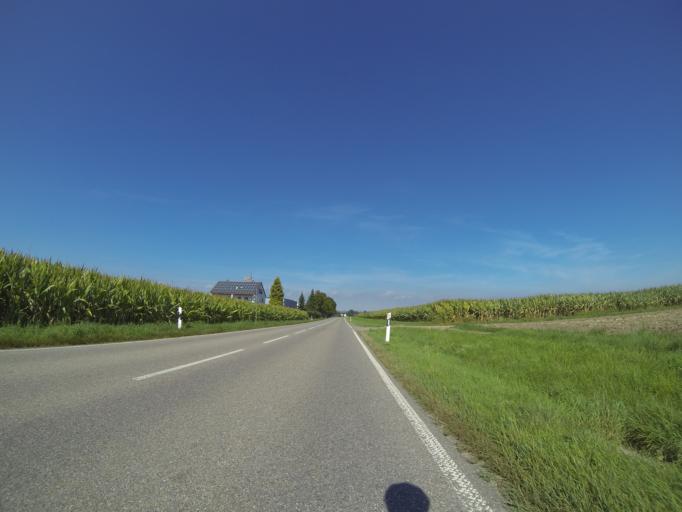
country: DE
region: Baden-Wuerttemberg
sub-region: Tuebingen Region
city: Erbach
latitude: 48.3013
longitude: 9.9082
